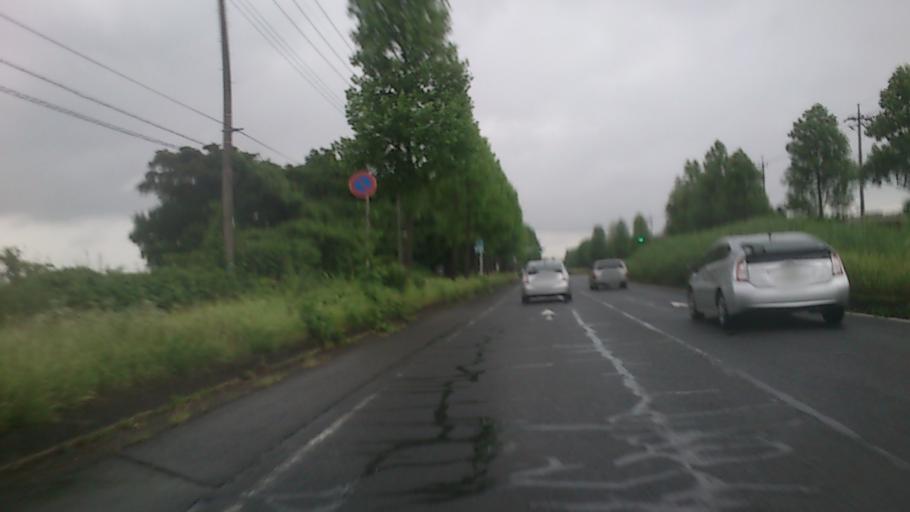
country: JP
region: Ibaraki
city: Naka
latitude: 36.0176
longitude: 140.1438
